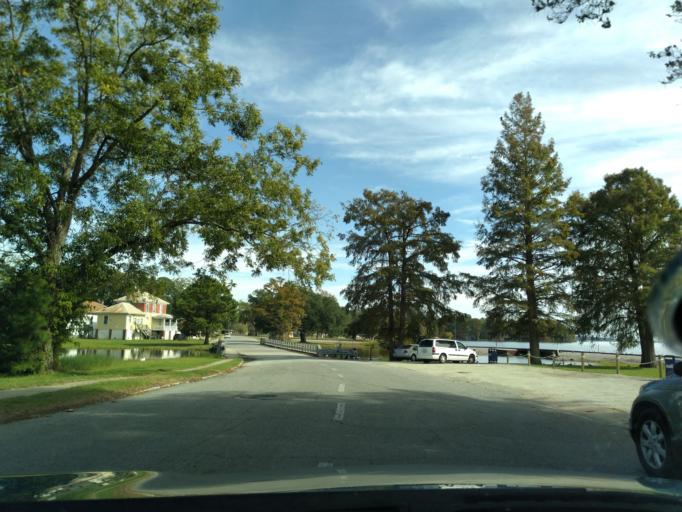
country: US
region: North Carolina
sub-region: Beaufort County
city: Washington
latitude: 35.5375
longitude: -77.0448
